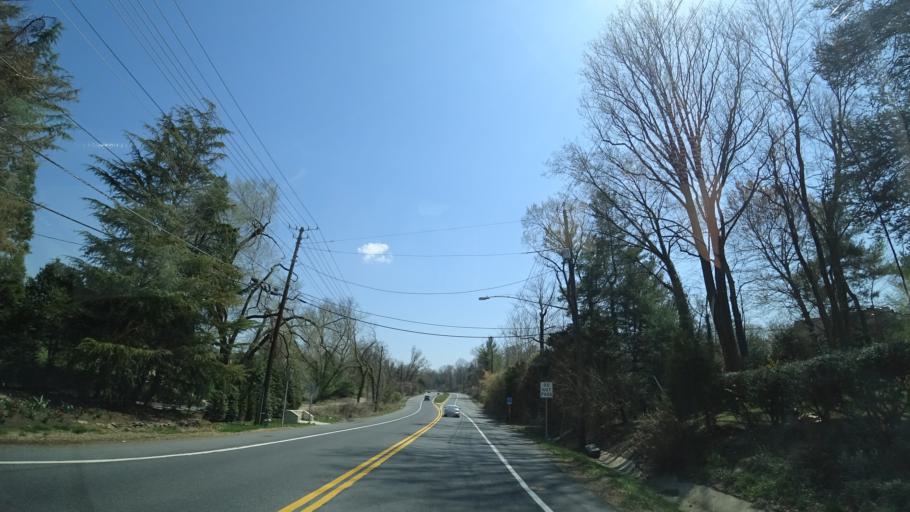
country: US
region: Maryland
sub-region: Montgomery County
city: Cabin John
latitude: 39.0120
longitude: -77.1558
